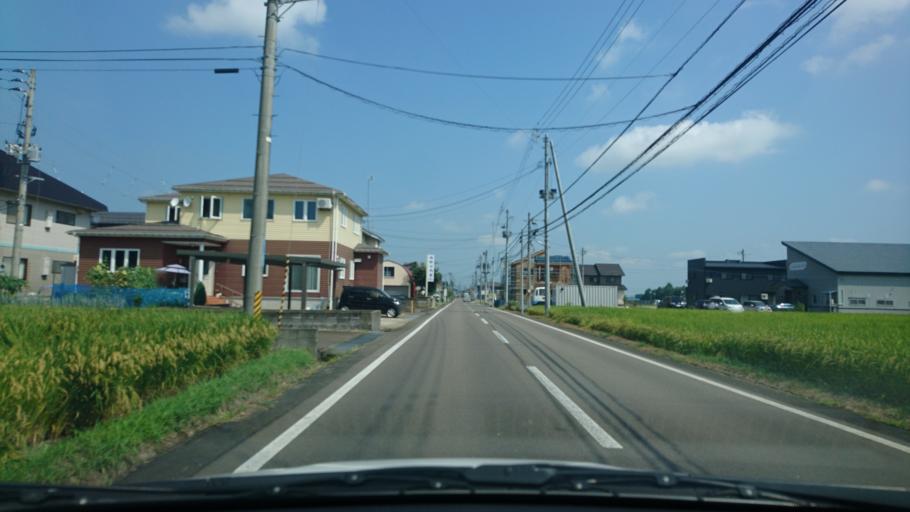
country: JP
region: Niigata
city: Arai
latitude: 37.0465
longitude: 138.2641
